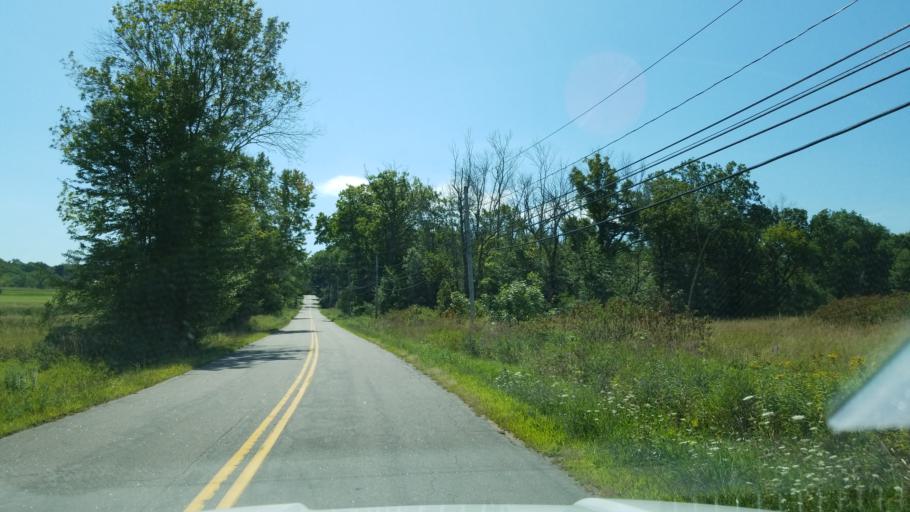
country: US
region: Connecticut
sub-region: Hartford County
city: Tariffville
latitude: 41.8606
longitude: -72.7623
